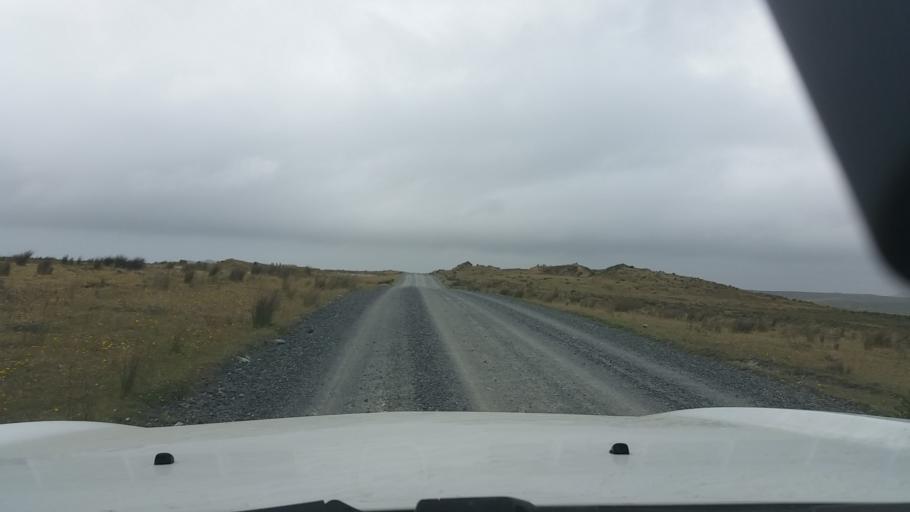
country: NZ
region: Chatham Islands
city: Waitangi
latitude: -43.8040
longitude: -176.6978
